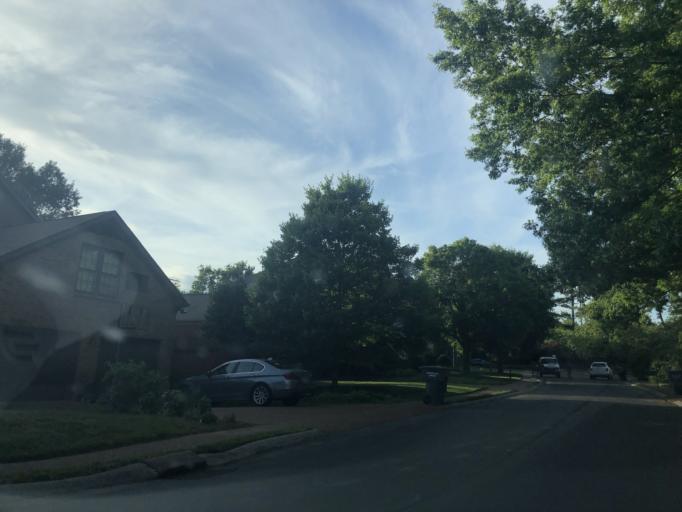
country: US
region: Tennessee
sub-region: Davidson County
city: Belle Meade
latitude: 36.0603
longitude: -86.9194
